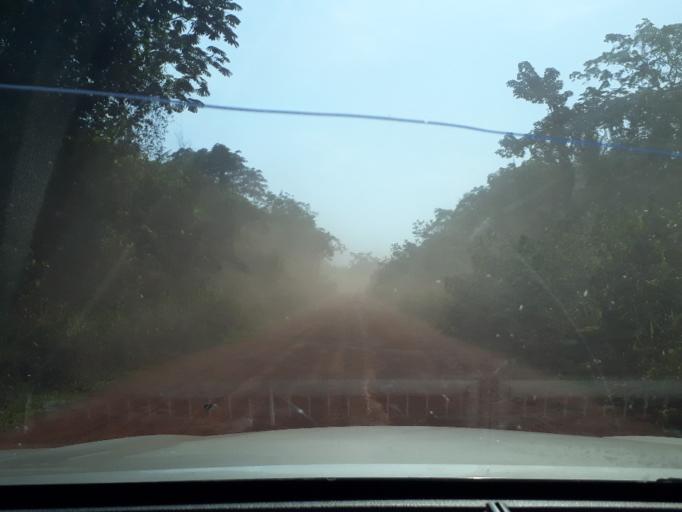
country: CD
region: Eastern Province
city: Kisangani
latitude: 0.4626
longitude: 25.4551
